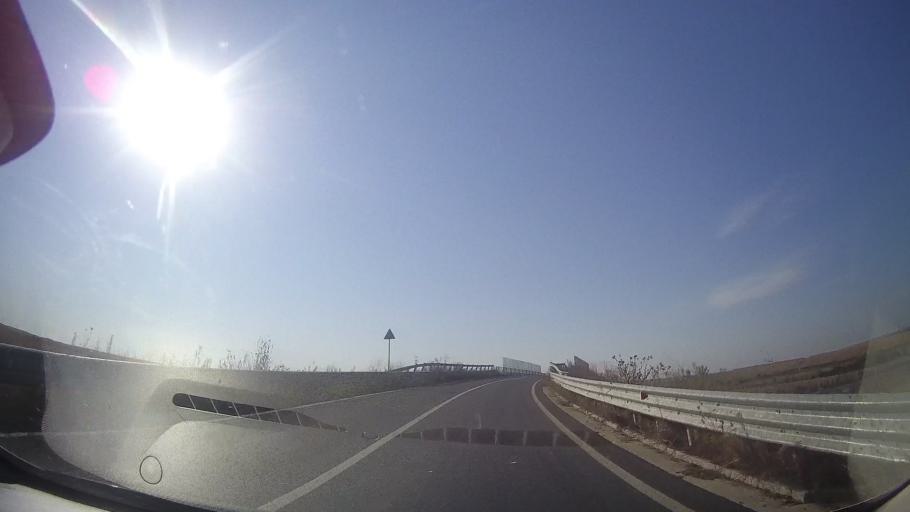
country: RO
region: Timis
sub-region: Comuna Topolovatu Mare
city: Topolovatu Mare
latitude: 45.8065
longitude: 21.5848
